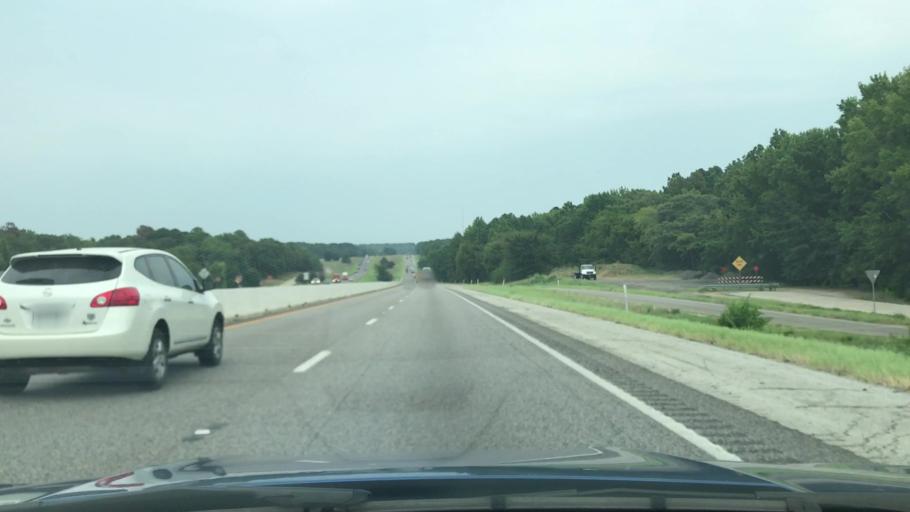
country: US
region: Texas
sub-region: Smith County
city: Lindale
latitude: 32.4682
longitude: -95.3671
